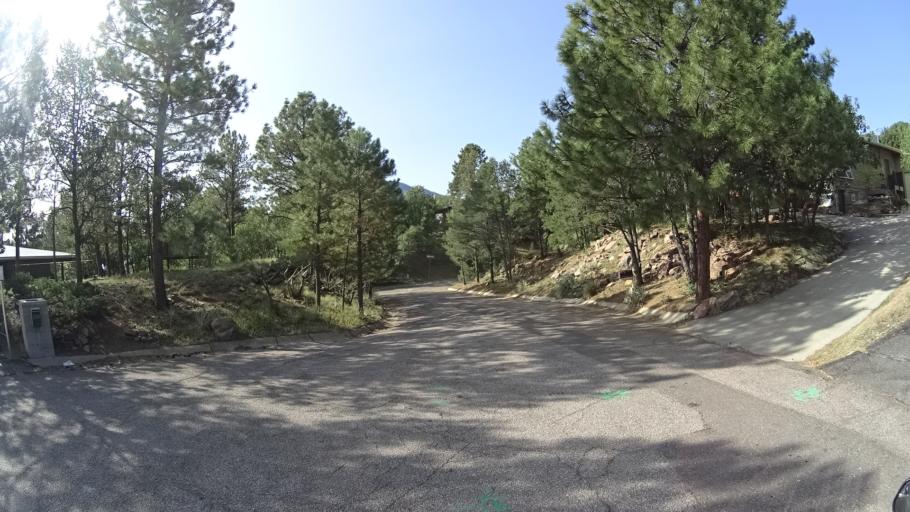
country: US
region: Colorado
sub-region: El Paso County
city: Colorado Springs
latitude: 38.8111
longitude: -104.8604
